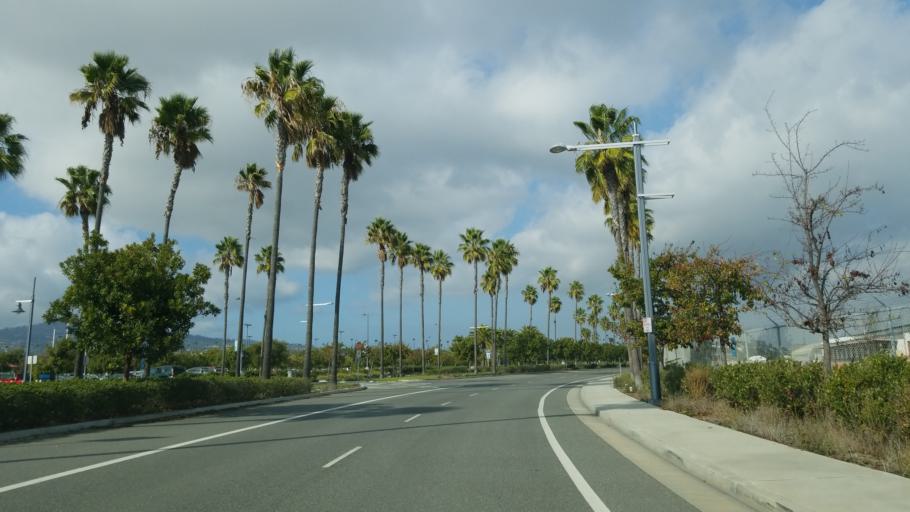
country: US
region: California
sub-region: Los Angeles County
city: San Pedro
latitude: 33.7223
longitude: -118.2765
